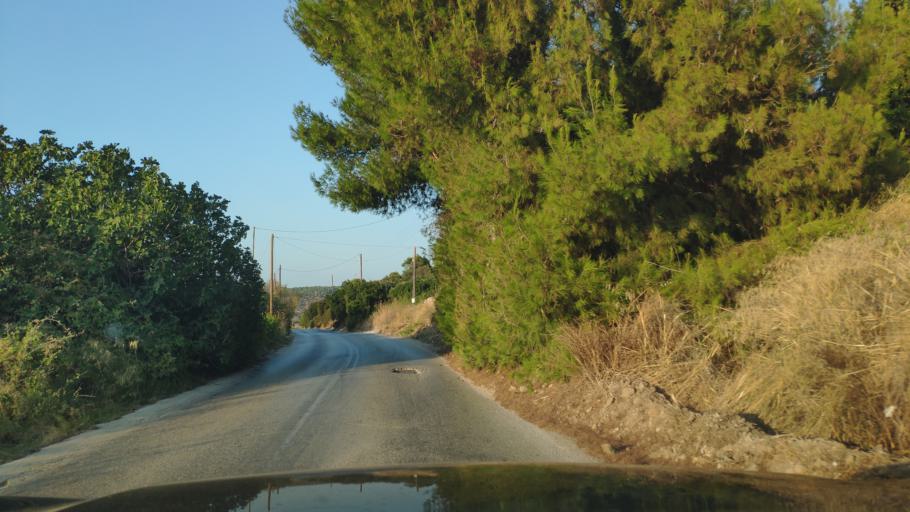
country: GR
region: Attica
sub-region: Nomarchia Anatolikis Attikis
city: Limin Mesoyaias
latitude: 37.9158
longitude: 23.9739
